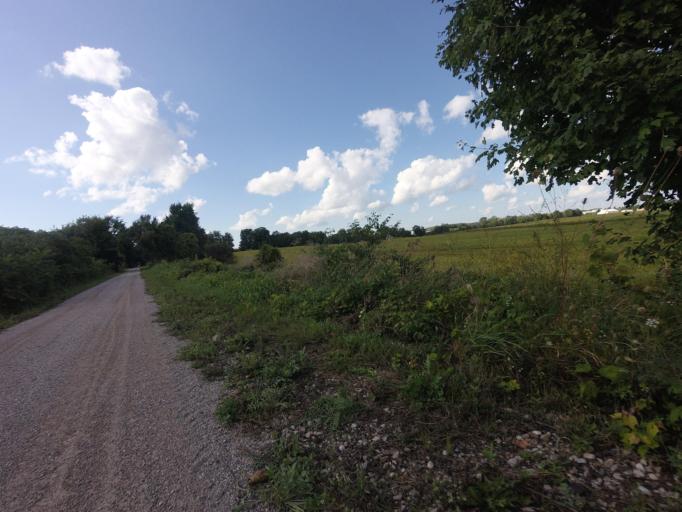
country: CA
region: Ontario
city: Goderich
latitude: 43.7466
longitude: -81.4960
